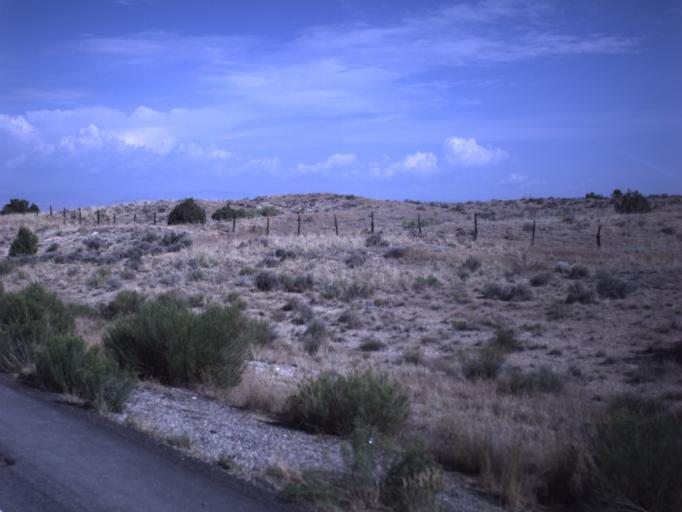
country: US
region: Utah
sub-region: Uintah County
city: Naples
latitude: 40.3271
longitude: -109.2714
